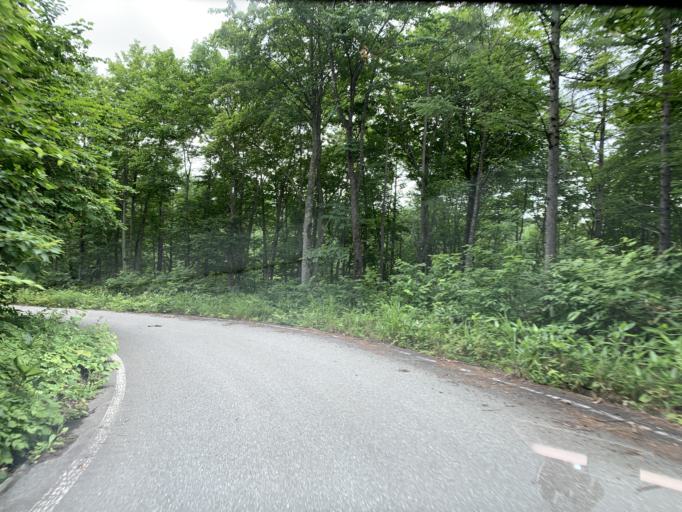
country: JP
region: Iwate
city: Ichinoseki
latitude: 38.9435
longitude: 140.8746
